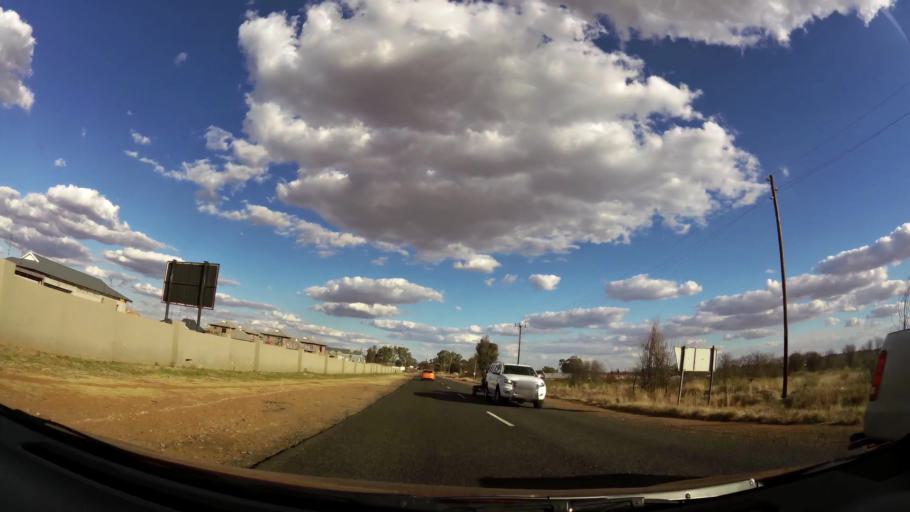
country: ZA
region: North-West
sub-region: Dr Kenneth Kaunda District Municipality
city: Potchefstroom
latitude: -26.6683
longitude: 27.1057
